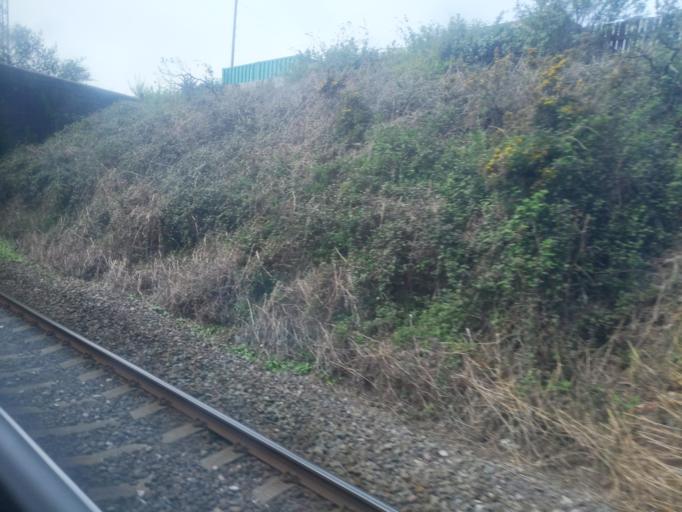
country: GB
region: England
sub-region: Cornwall
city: Redruth
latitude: 50.2253
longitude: -5.2549
